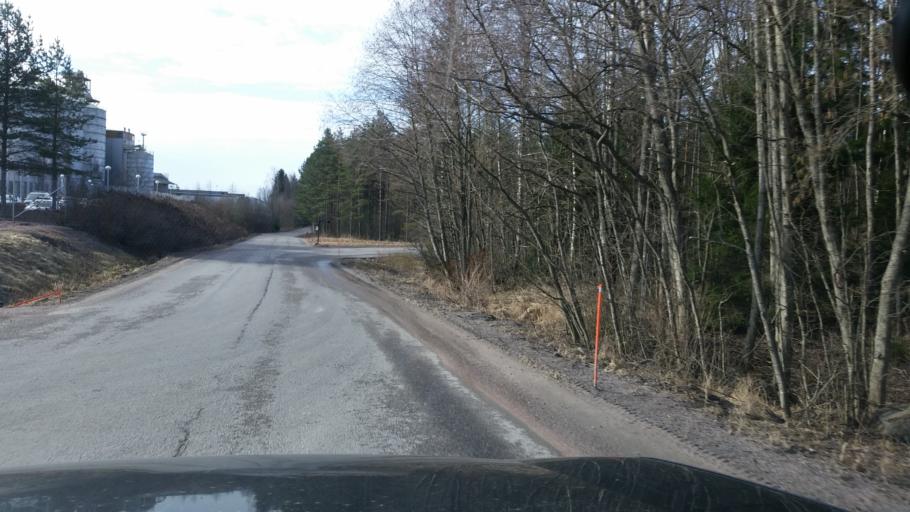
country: FI
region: Uusimaa
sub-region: Helsinki
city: Kirkkonummi
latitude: 60.0912
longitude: 24.3755
